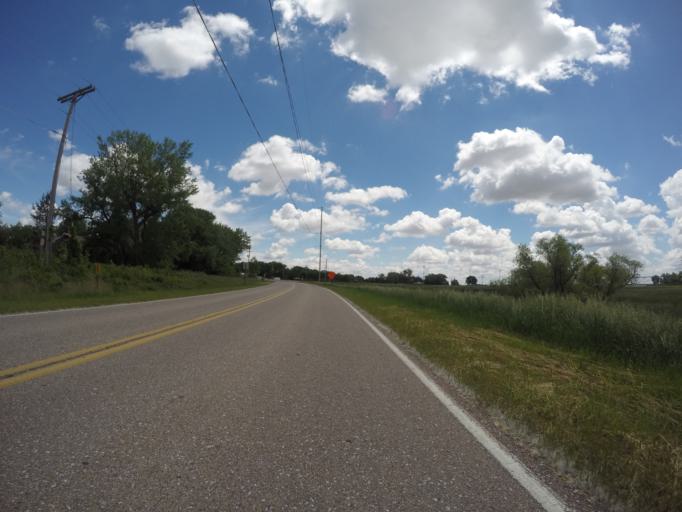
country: US
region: Nebraska
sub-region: Buffalo County
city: Kearney
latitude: 40.6527
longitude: -99.0875
